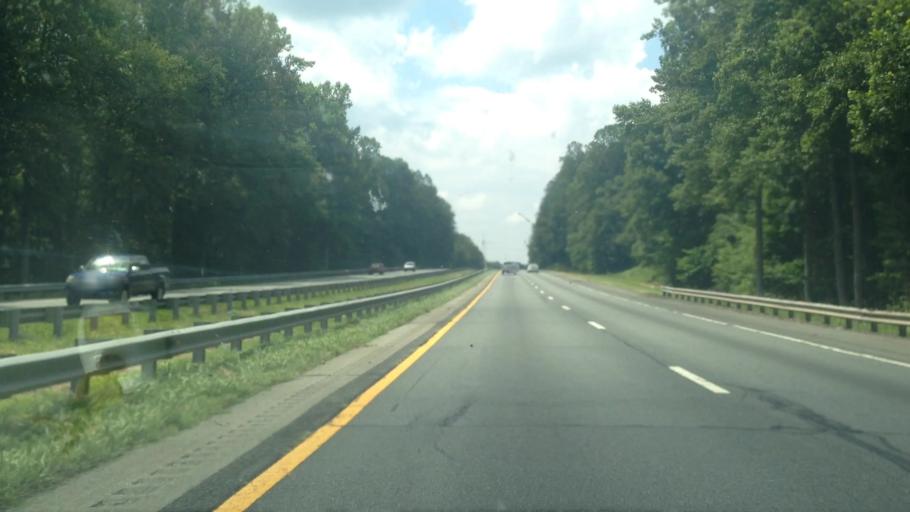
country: US
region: North Carolina
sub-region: Forsyth County
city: Tobaccoville
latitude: 36.2331
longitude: -80.3323
